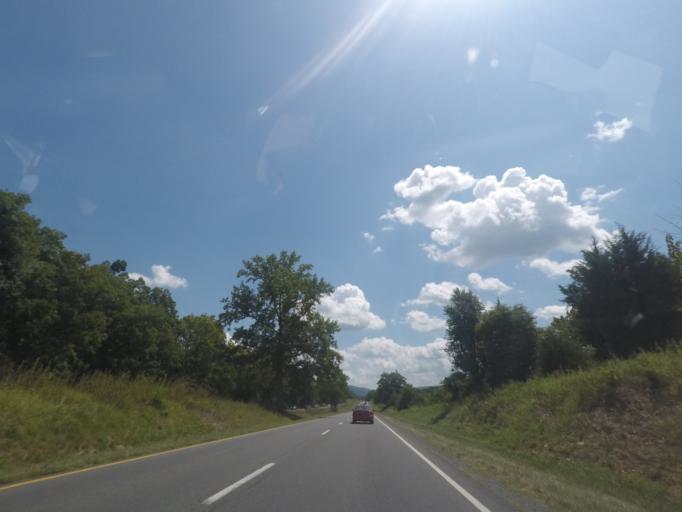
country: US
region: Virginia
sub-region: Warren County
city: Shenandoah Farms
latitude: 39.0678
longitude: -78.0587
